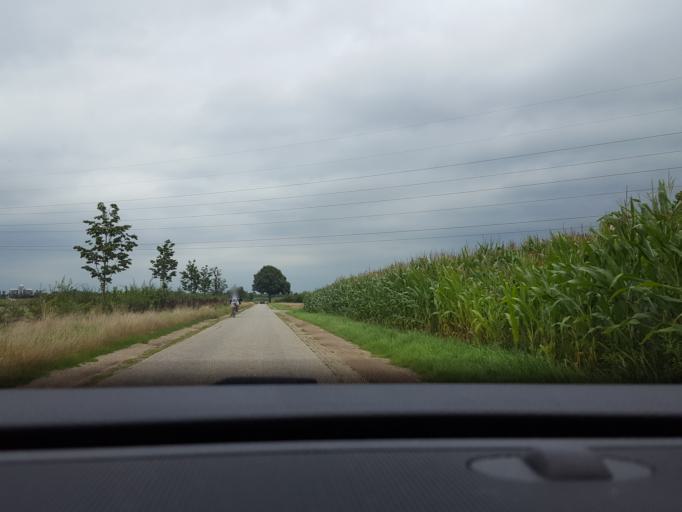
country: NL
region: Gelderland
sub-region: Gemeente Zutphen
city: Leesten
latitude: 52.1165
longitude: 6.2256
